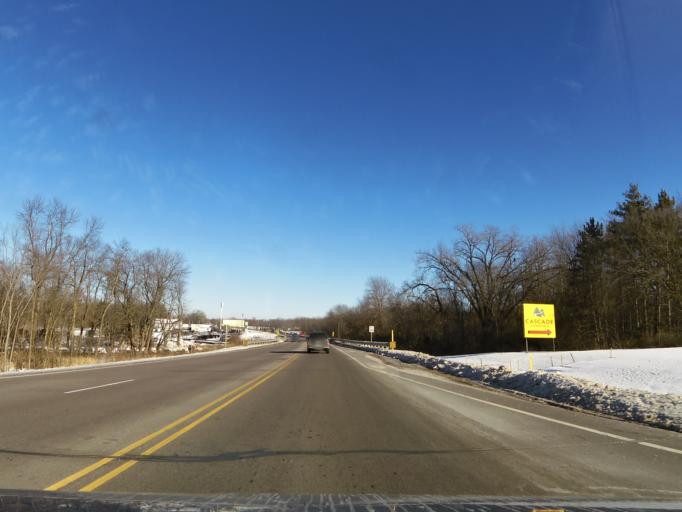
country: US
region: Wisconsin
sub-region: Columbia County
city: Portage
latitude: 43.5086
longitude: -89.5327
